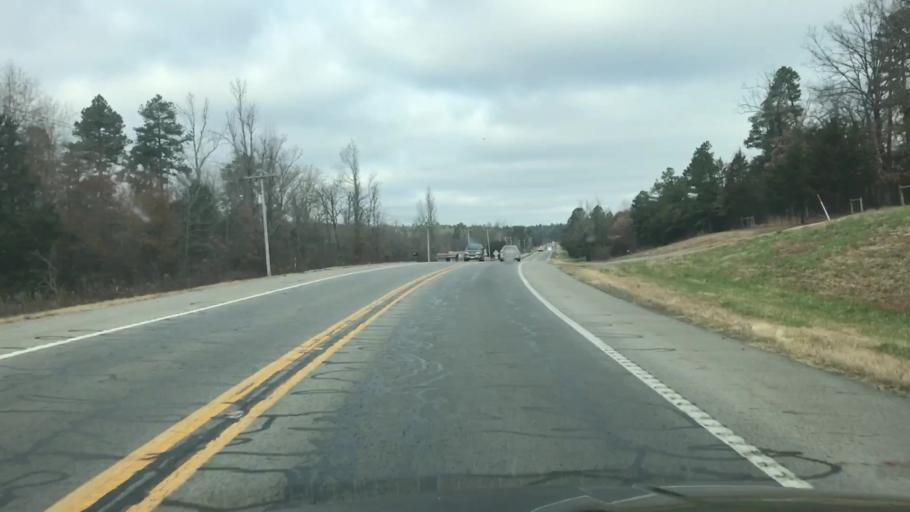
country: US
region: Arkansas
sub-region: Scott County
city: Waldron
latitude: 34.8257
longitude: -94.0381
